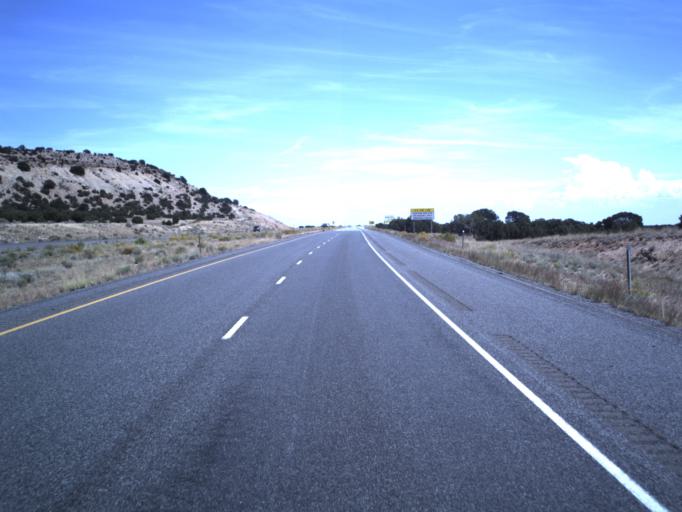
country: US
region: Utah
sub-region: Emery County
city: Castle Dale
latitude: 38.9052
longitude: -110.5484
